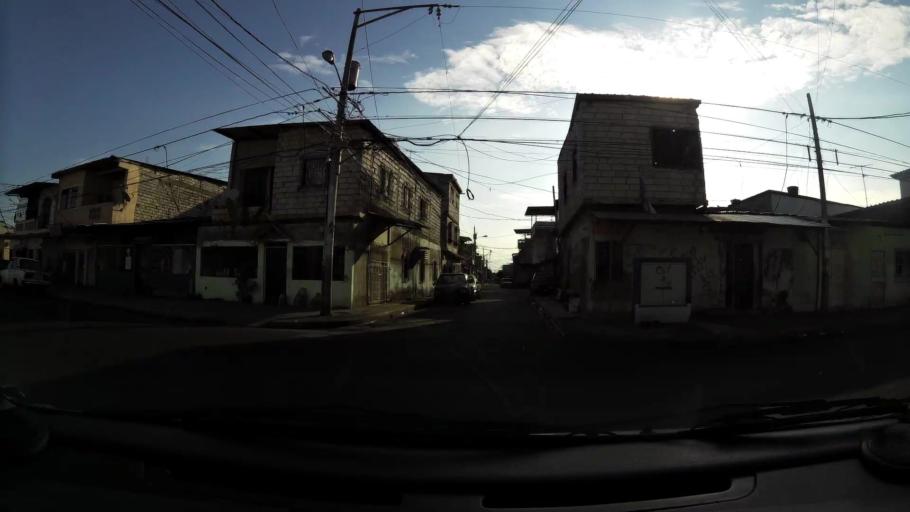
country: EC
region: Guayas
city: Guayaquil
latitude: -2.2272
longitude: -79.9103
